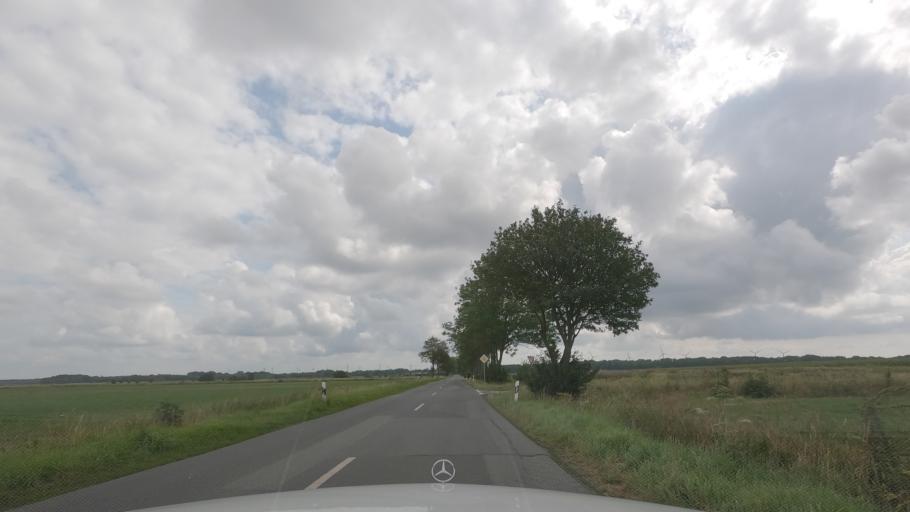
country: DE
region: Lower Saxony
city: Uthlede
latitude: 53.3097
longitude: 8.5514
